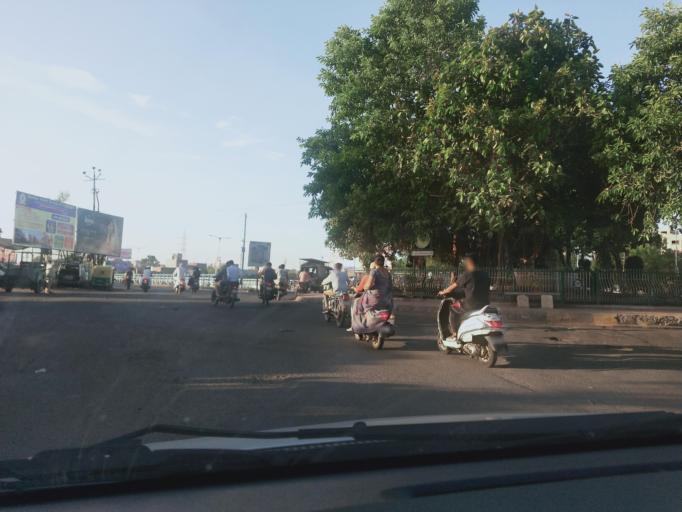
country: IN
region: Gujarat
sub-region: Bhavnagar
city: Bhavnagar
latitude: 21.7419
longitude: 72.1493
